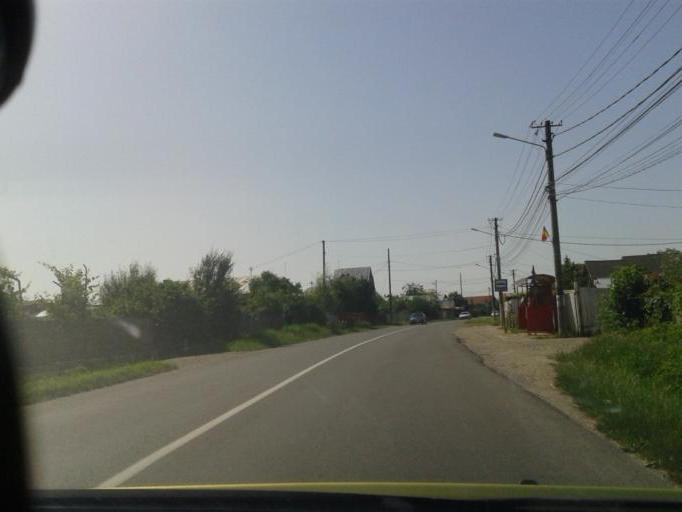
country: RO
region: Prahova
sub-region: Comuna Paulesti
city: Gageni
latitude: 45.0306
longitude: 25.9431
